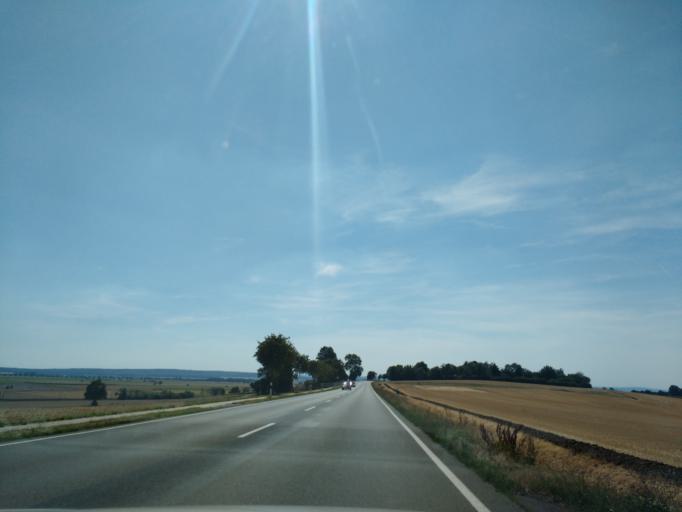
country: DE
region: Lower Saxony
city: Schellerten
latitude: 52.2037
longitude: 10.1652
